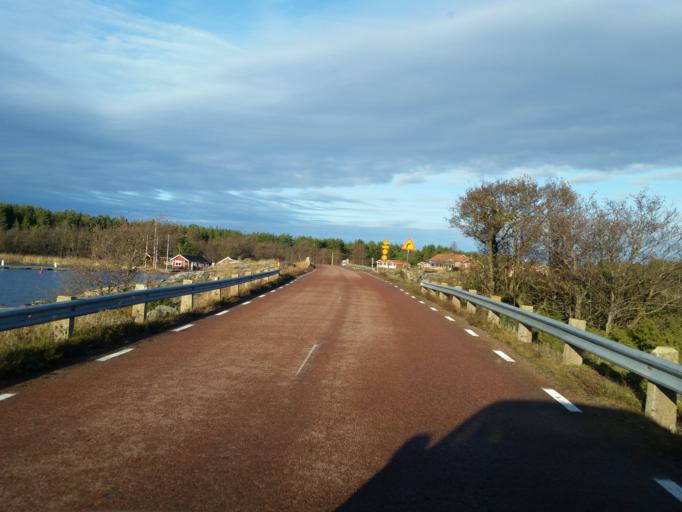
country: AX
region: Alands skaergard
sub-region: Kumlinge
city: Kumlinge
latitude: 60.2557
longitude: 20.7377
